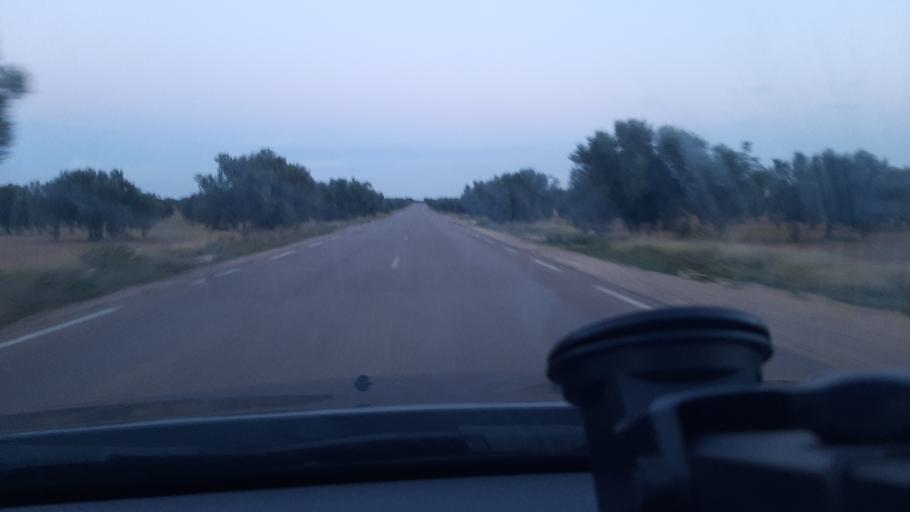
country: TN
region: Al Mahdiyah
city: Shurban
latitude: 35.0330
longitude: 10.5089
